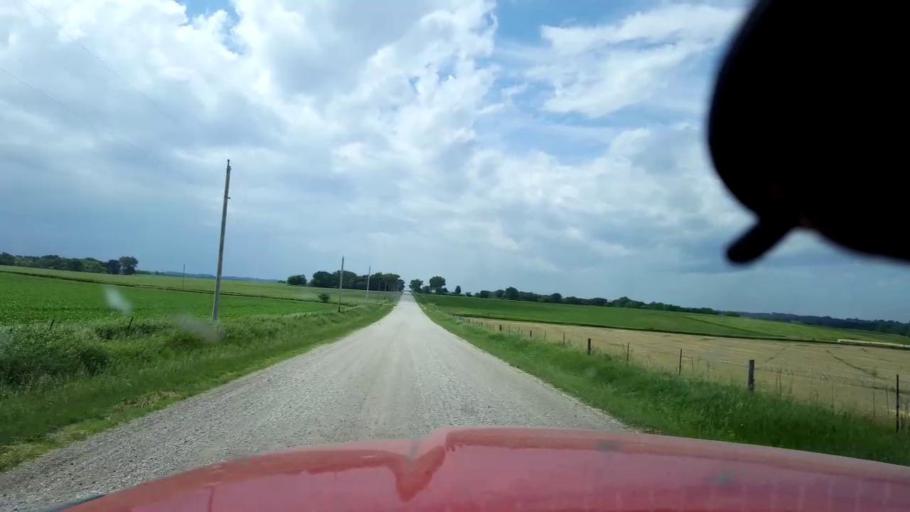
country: US
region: Iowa
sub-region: Cherokee County
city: Cherokee
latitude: 42.8164
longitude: -95.5345
